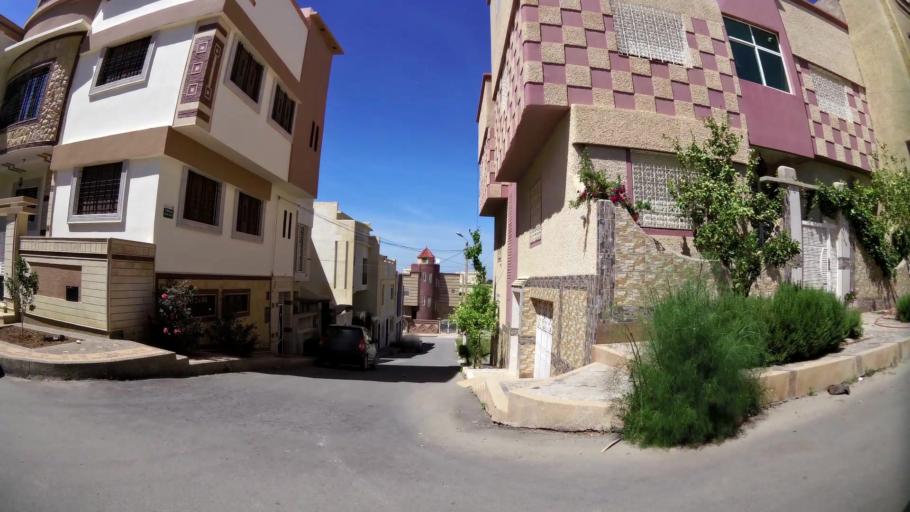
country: MA
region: Oriental
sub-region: Oujda-Angad
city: Oujda
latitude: 34.6467
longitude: -1.9081
